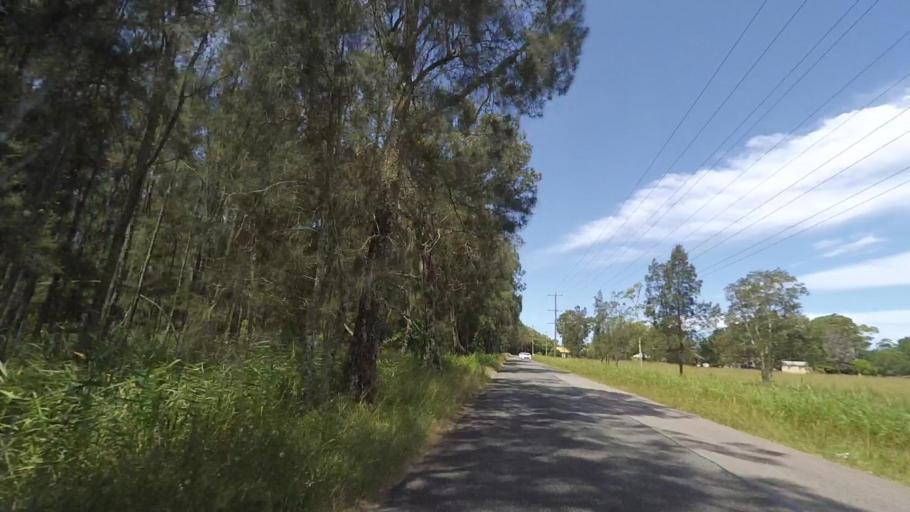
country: AU
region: New South Wales
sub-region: Port Stephens Shire
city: Port Stephens
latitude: -32.7665
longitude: 152.0082
